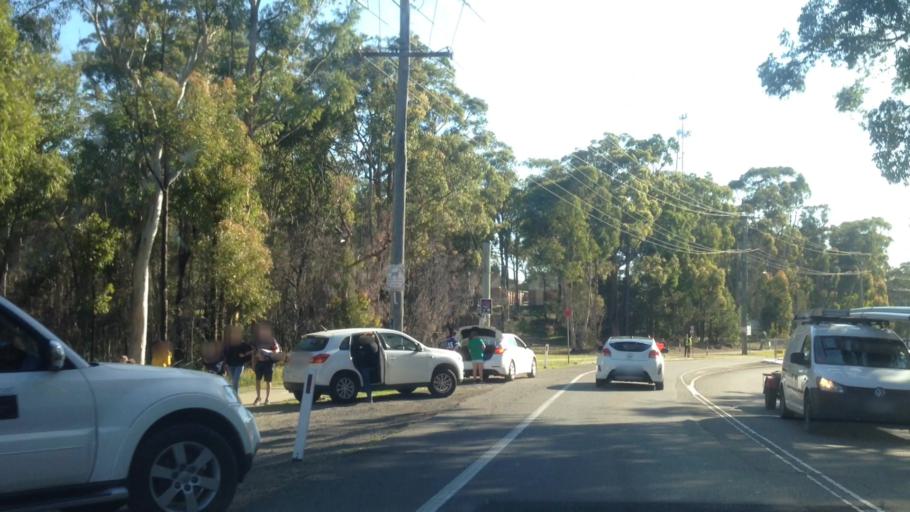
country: AU
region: New South Wales
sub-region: Lake Macquarie Shire
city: Dora Creek
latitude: -33.1129
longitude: 151.5181
